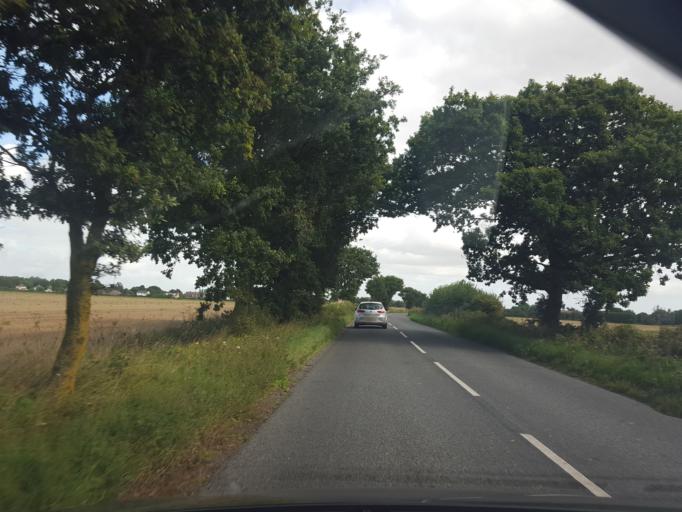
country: GB
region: England
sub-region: Essex
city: Mistley
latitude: 51.9252
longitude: 1.0892
